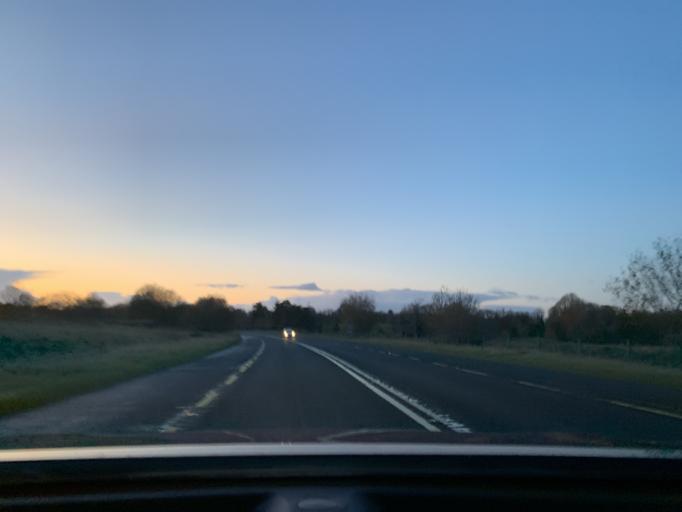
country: IE
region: Connaught
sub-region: County Leitrim
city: Carrick-on-Shannon
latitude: 53.9572
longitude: -8.1628
